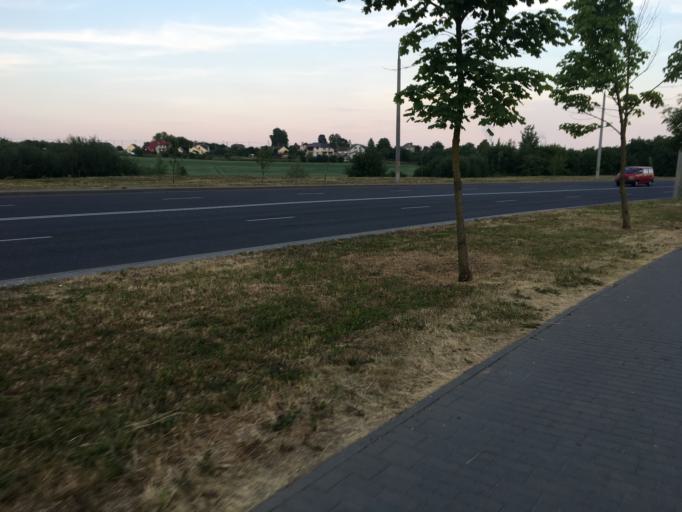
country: BY
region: Grodnenskaya
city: Hrodna
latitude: 53.7101
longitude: 23.8602
